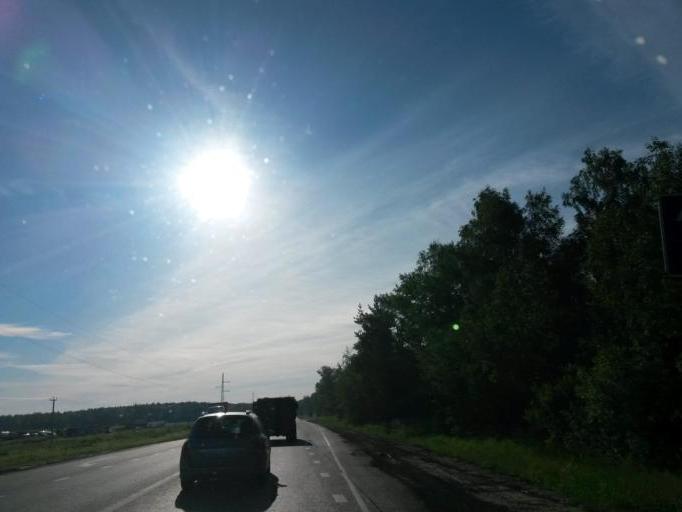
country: RU
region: Moskovskaya
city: Domodedovo
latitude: 55.3315
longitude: 37.6703
